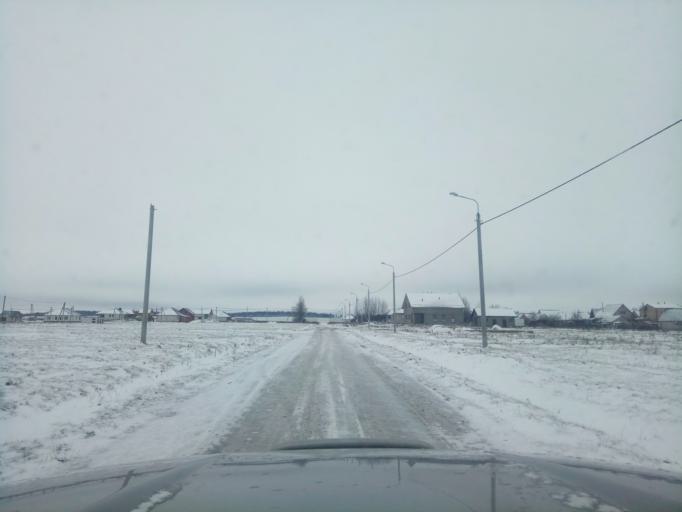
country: BY
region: Minsk
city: Kapyl'
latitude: 53.1616
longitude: 27.0815
